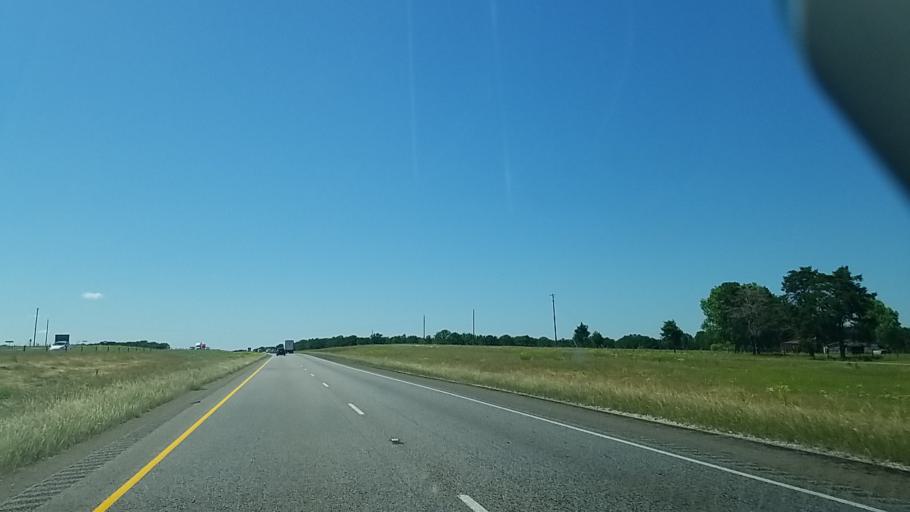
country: US
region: Texas
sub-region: Freestone County
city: Fairfield
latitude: 31.7598
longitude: -96.2085
